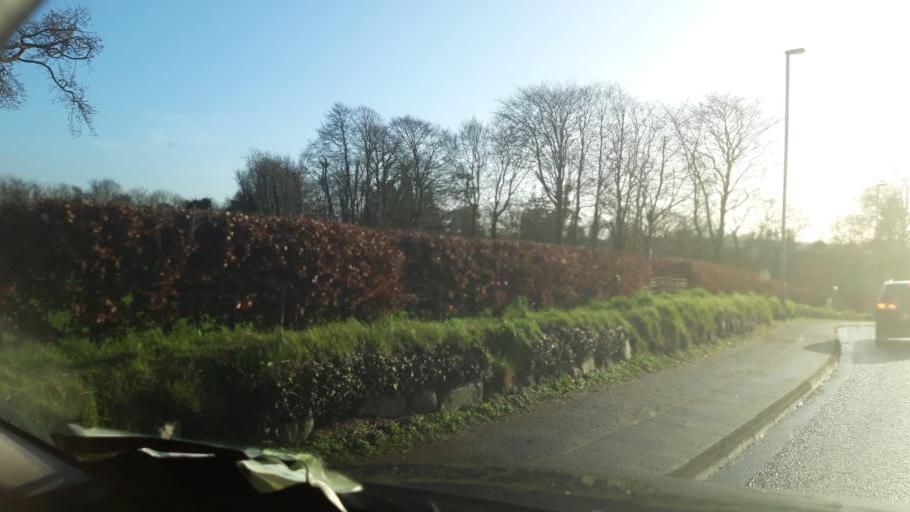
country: GB
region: Northern Ireland
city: Garvagh
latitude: 54.9885
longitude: -6.6855
